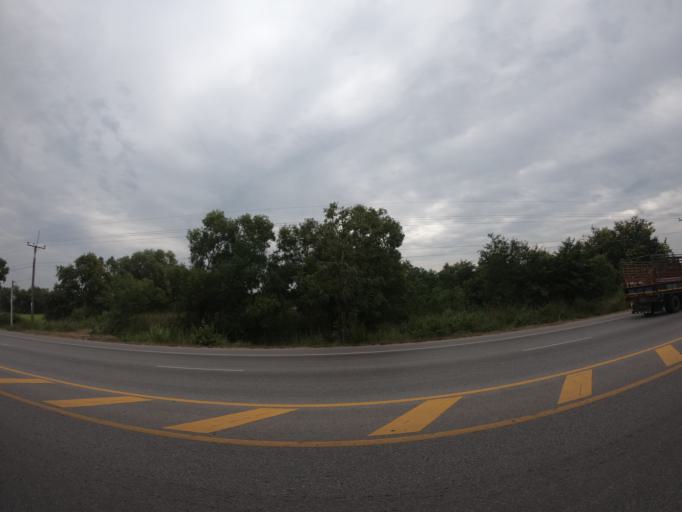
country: TH
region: Roi Et
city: Thawat Buri
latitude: 16.0828
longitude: 103.7292
